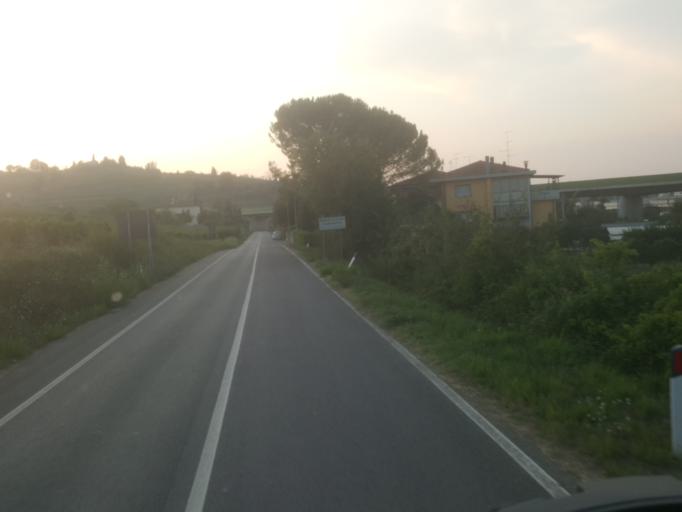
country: IT
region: Tuscany
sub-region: Province of Florence
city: Certaldo
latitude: 43.5307
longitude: 11.0373
